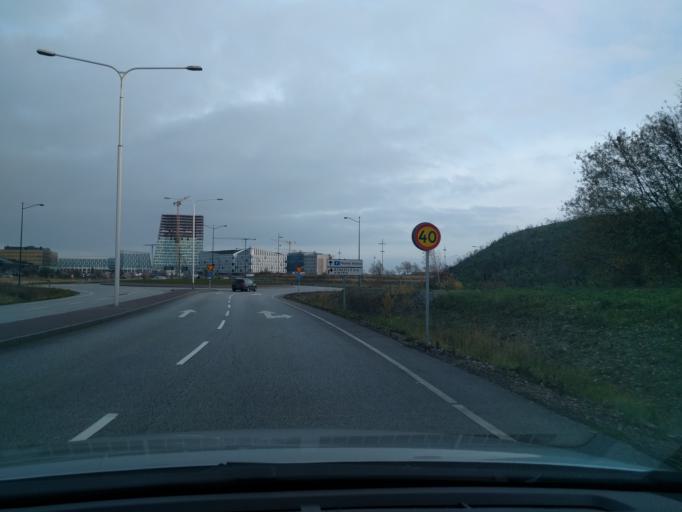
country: SE
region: Skane
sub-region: Malmo
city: Bunkeflostrand
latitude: 55.5612
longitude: 12.9704
